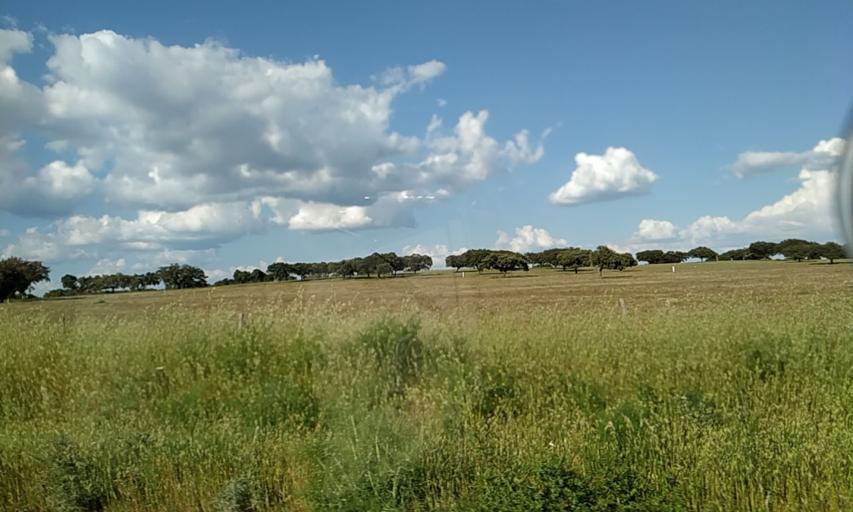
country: PT
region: Portalegre
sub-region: Portalegre
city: Urra
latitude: 39.1496
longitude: -7.4535
